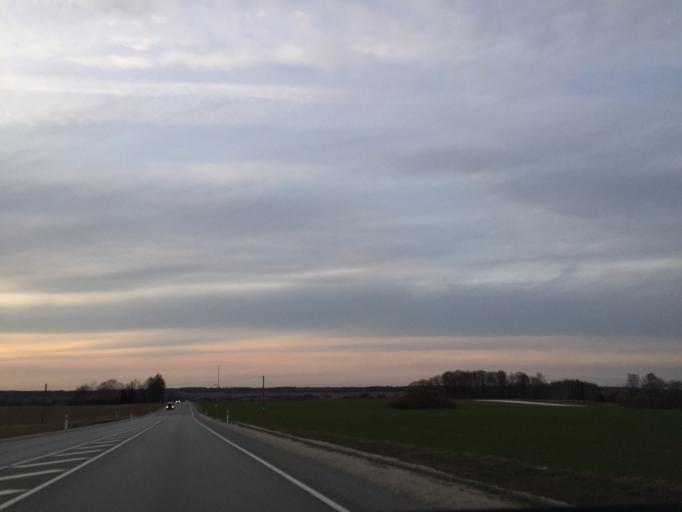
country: EE
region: Tartu
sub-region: UElenurme vald
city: Ulenurme
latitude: 58.2407
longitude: 26.6871
